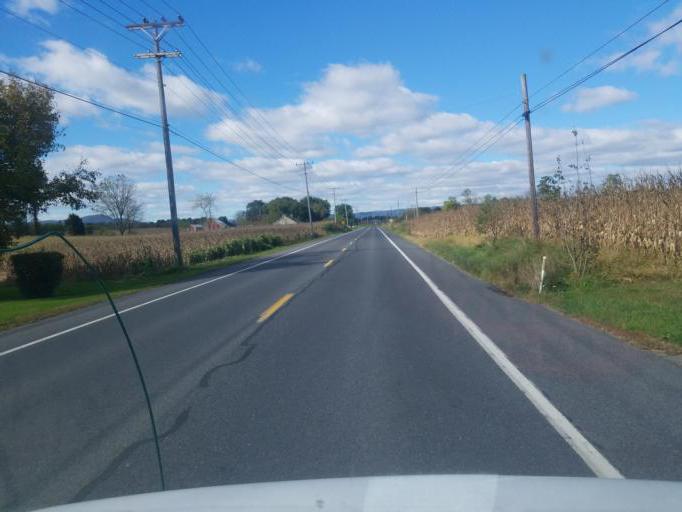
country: US
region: Pennsylvania
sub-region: Franklin County
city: Mercersburg
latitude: 39.8023
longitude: -77.8434
